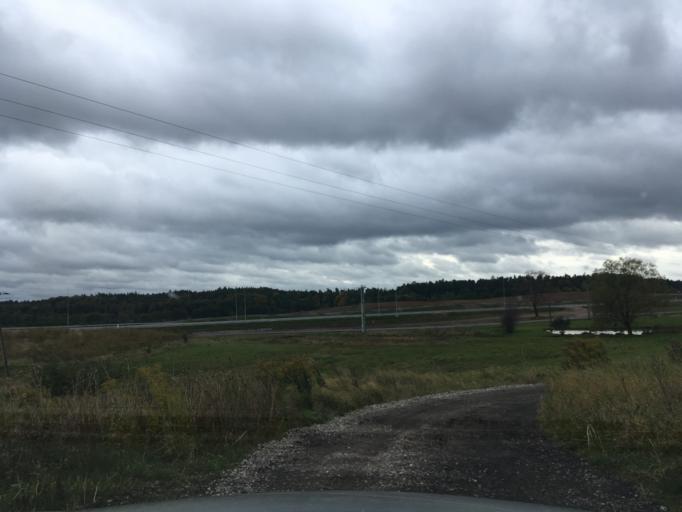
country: PL
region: Pomeranian Voivodeship
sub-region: Powiat koscierski
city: Koscierzyna
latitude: 54.1133
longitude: 17.9997
